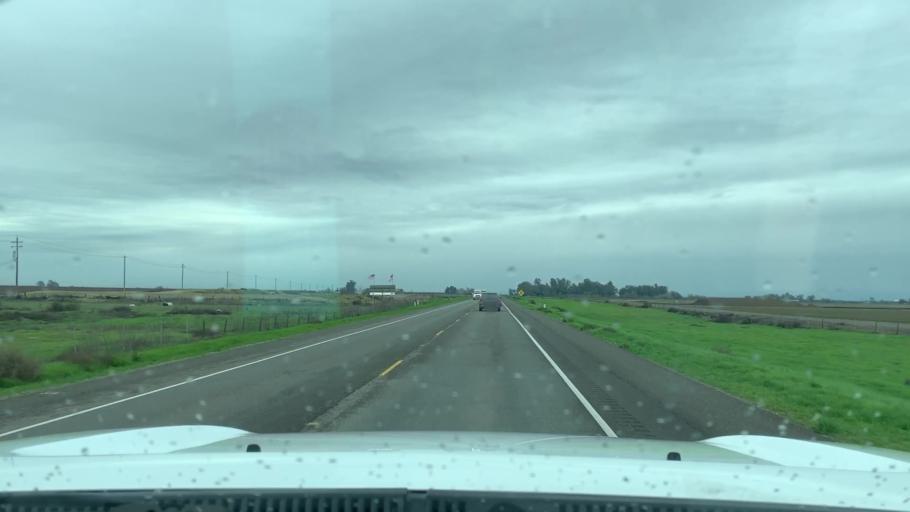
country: US
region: California
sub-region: Fresno County
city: Riverdale
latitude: 36.4496
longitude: -119.7975
